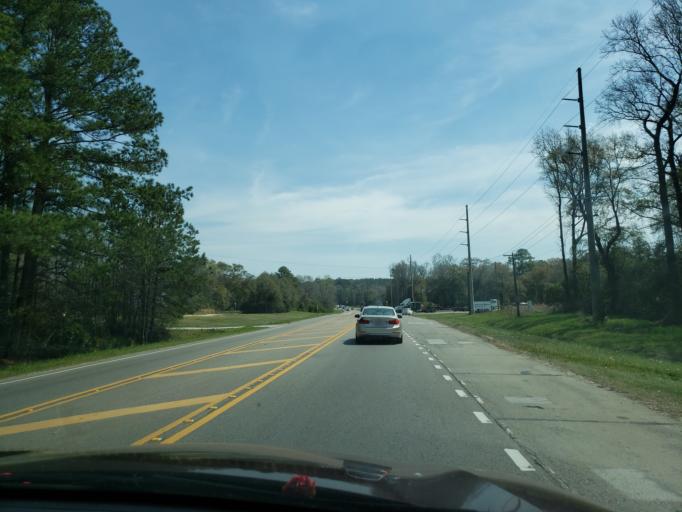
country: US
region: Alabama
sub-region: Autauga County
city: Prattville
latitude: 32.4369
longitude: -86.4694
